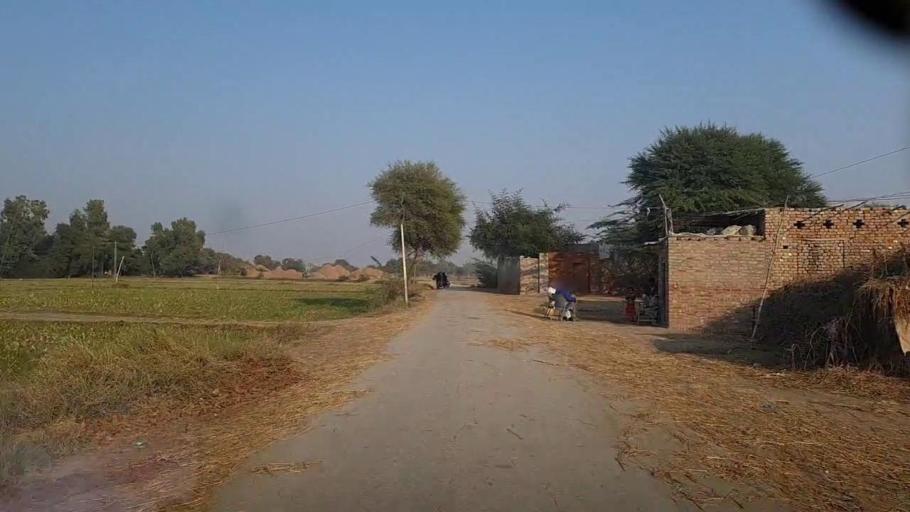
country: PK
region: Sindh
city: Jacobabad
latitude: 28.2383
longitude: 68.4865
